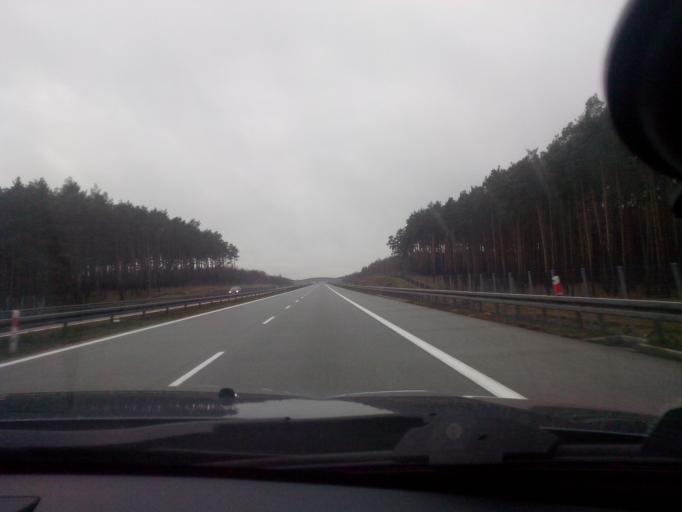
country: PL
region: Lubusz
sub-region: Powiat slubicki
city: Rzepin
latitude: 52.3343
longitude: 14.7450
